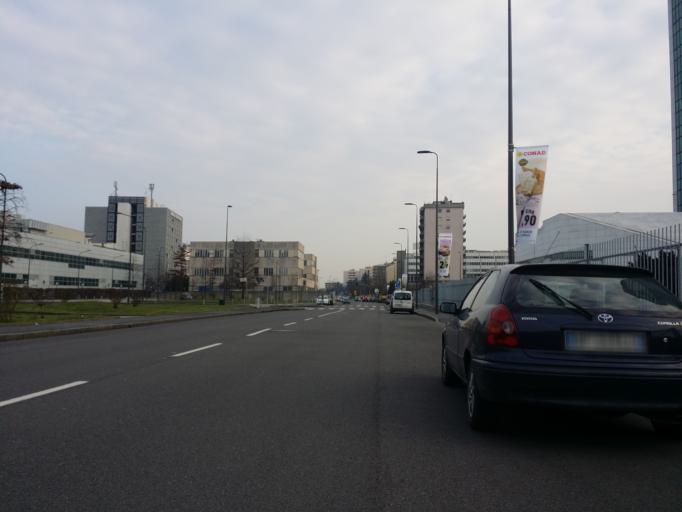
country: IT
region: Lombardy
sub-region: Citta metropolitana di Milano
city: Romano Banco
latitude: 45.4459
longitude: 9.1139
